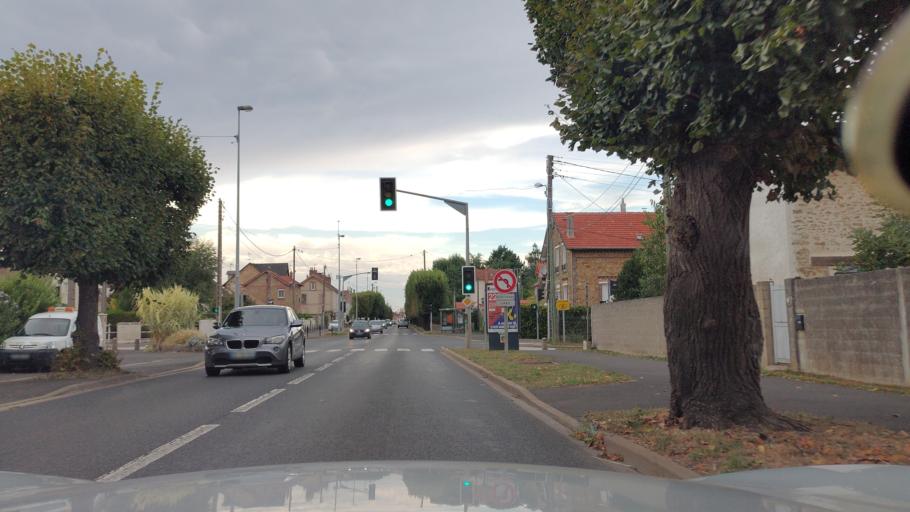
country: FR
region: Ile-de-France
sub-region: Departement de Seine-et-Marne
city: Guignes
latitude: 48.6330
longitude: 2.8054
